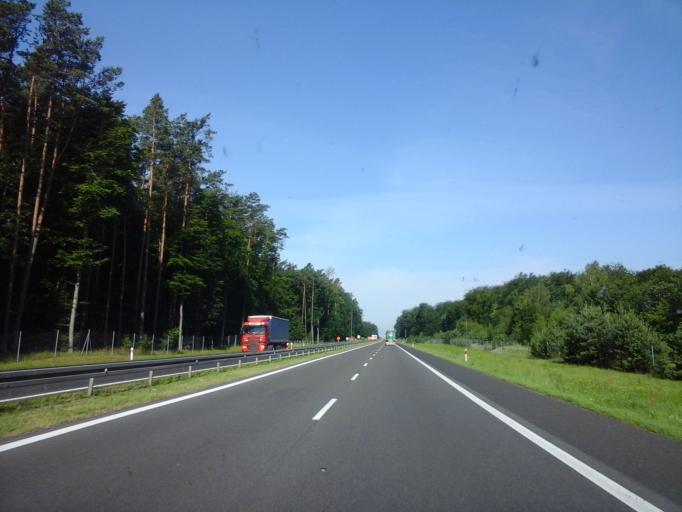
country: PL
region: West Pomeranian Voivodeship
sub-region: Powiat stargardzki
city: Kobylanka
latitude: 53.3524
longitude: 14.8152
